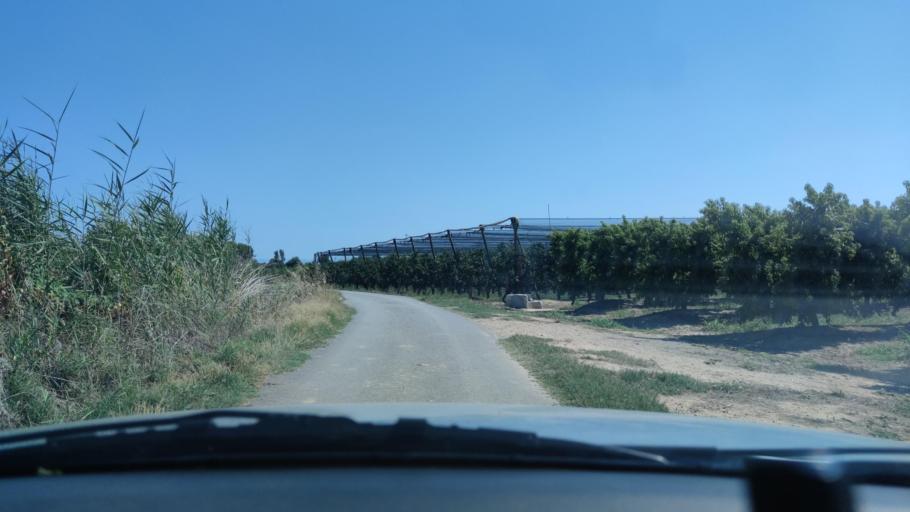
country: ES
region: Catalonia
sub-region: Provincia de Lleida
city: Alcoletge
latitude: 41.6707
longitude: 0.6614
